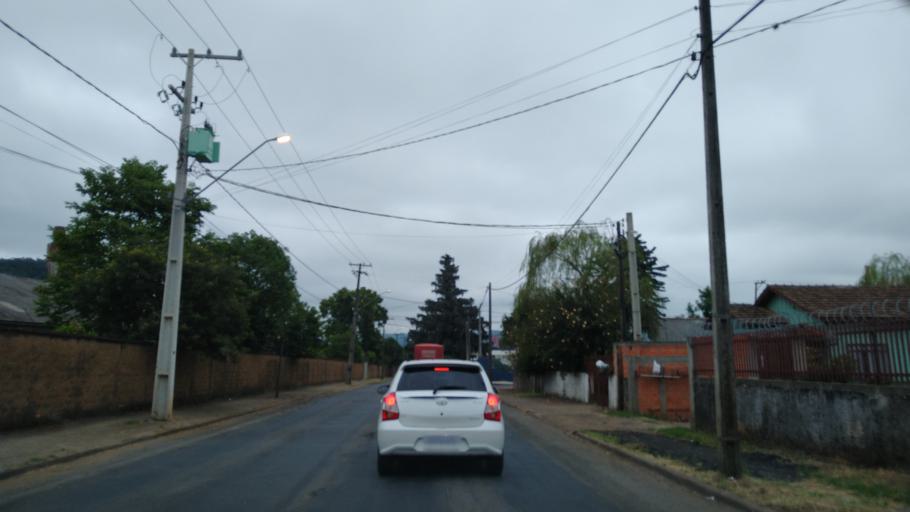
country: BR
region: Santa Catarina
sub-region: Porto Uniao
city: Porto Uniao
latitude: -26.2532
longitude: -51.0972
